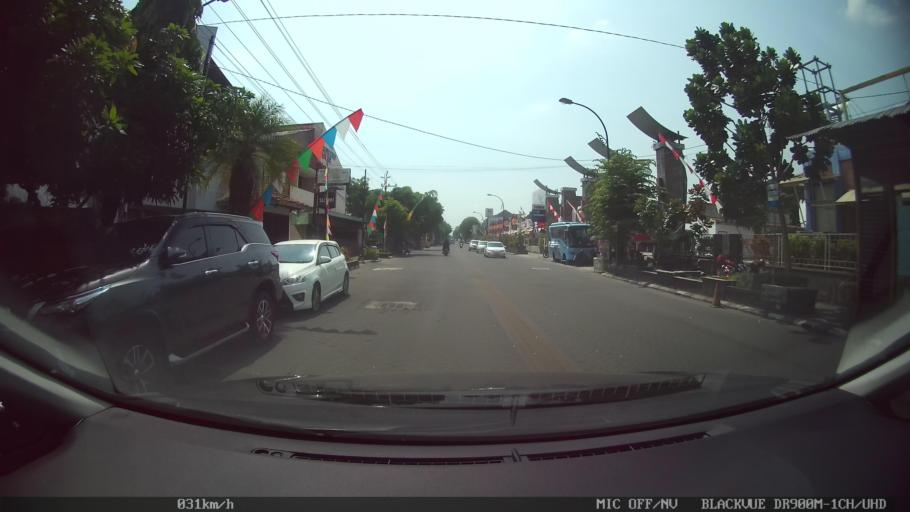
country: ID
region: Daerah Istimewa Yogyakarta
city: Yogyakarta
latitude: -7.8164
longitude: 110.3857
